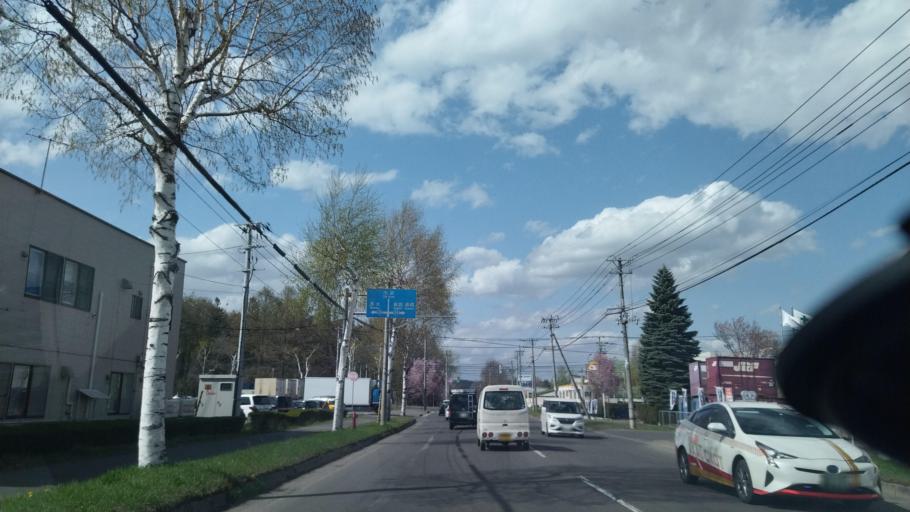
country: JP
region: Hokkaido
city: Obihiro
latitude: 42.9265
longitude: 143.1433
